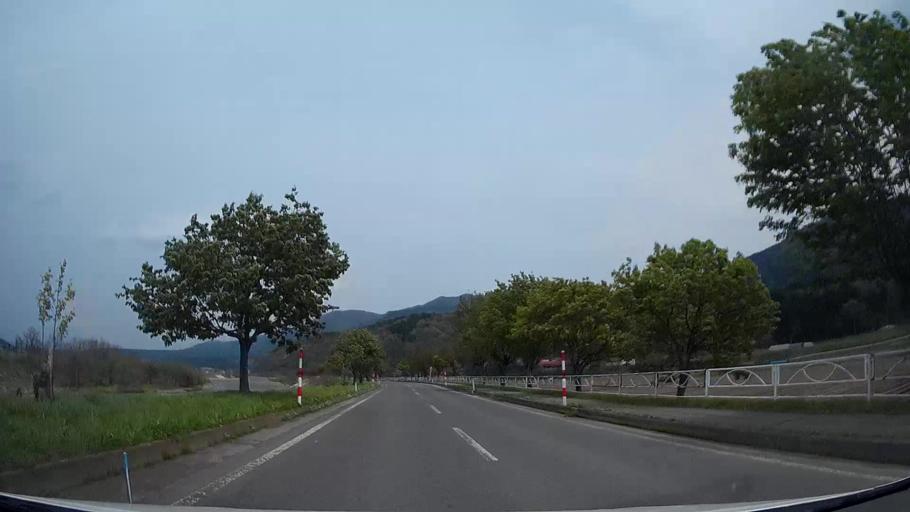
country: JP
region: Akita
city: Hanawa
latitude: 40.1218
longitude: 140.7850
